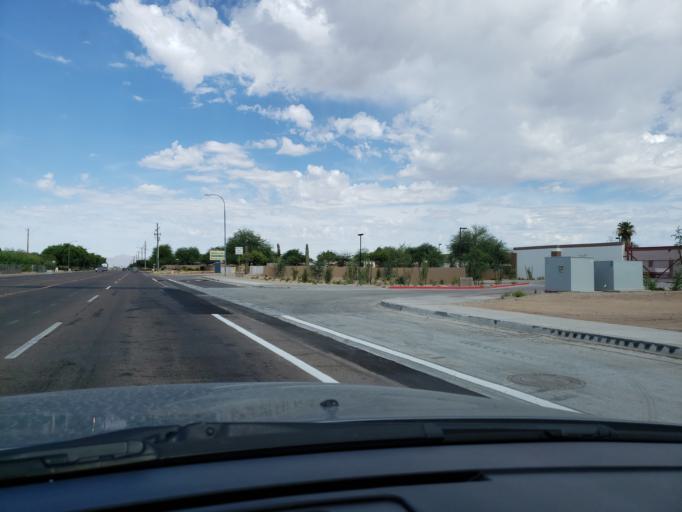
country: US
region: Arizona
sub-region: Maricopa County
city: Peoria
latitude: 33.5520
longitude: -112.2446
